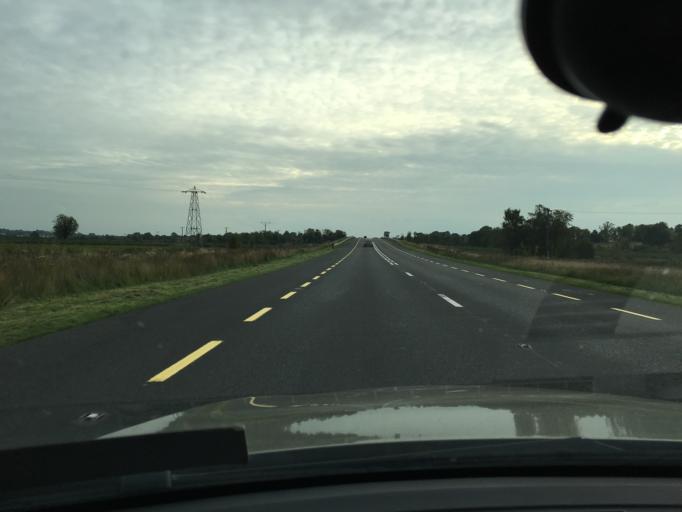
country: IE
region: Leinster
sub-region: An Longfort
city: Longford
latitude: 53.7387
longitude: -7.8150
